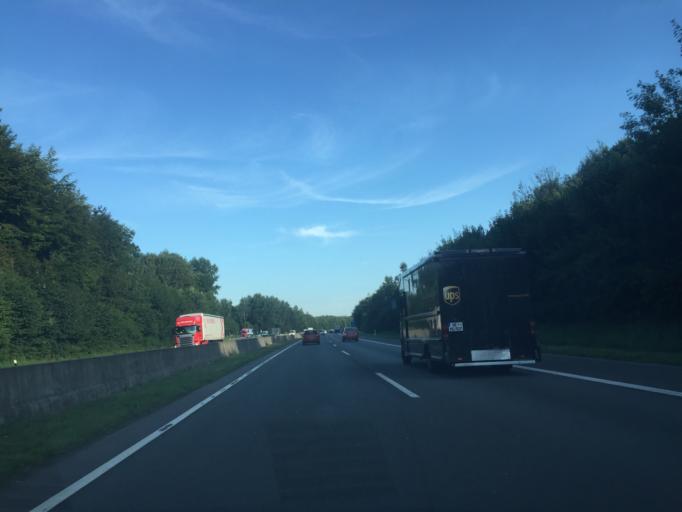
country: DE
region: North Rhine-Westphalia
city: Freudenberg
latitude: 50.9319
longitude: 7.8860
